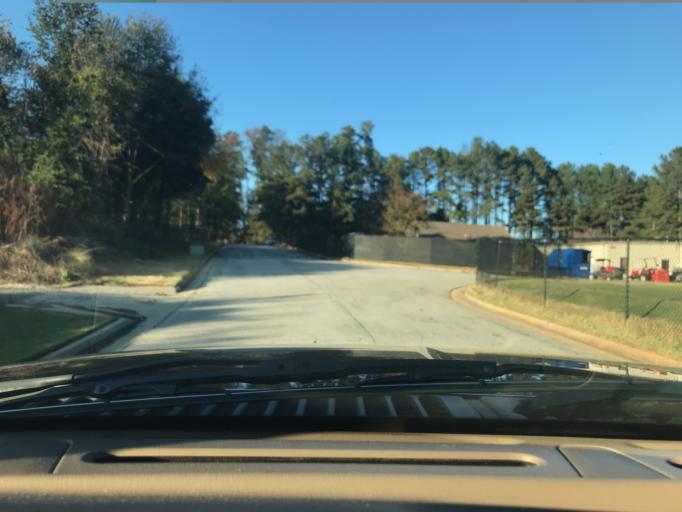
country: US
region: Georgia
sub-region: Fulton County
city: Johns Creek
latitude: 34.0321
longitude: -84.1840
